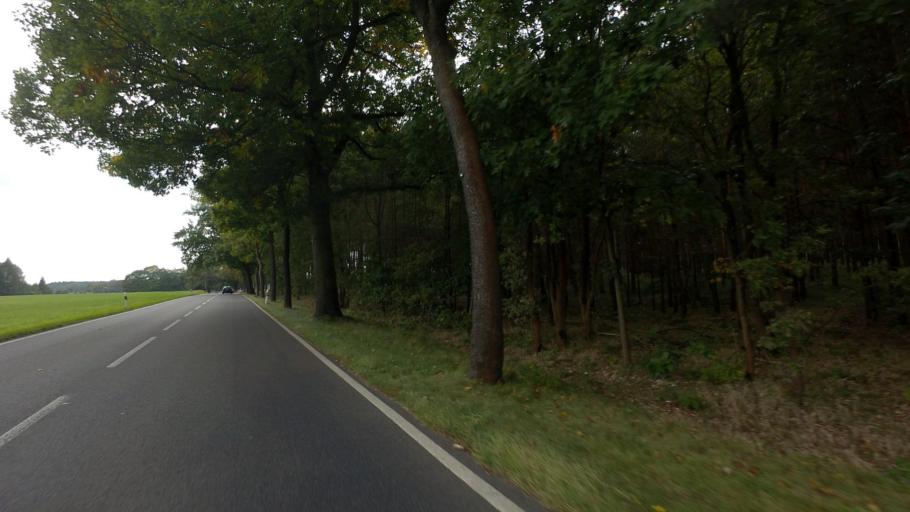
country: DE
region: Brandenburg
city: Sonnewalde
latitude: 51.7525
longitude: 13.6779
